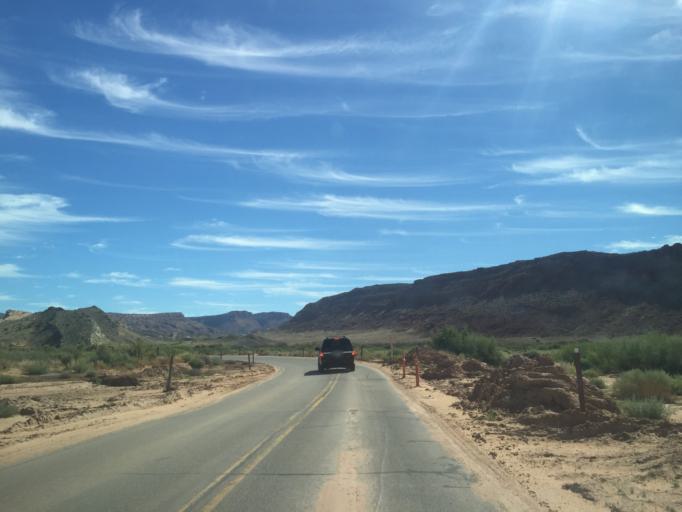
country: US
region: Utah
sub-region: Grand County
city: Moab
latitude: 38.7334
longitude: -109.5246
